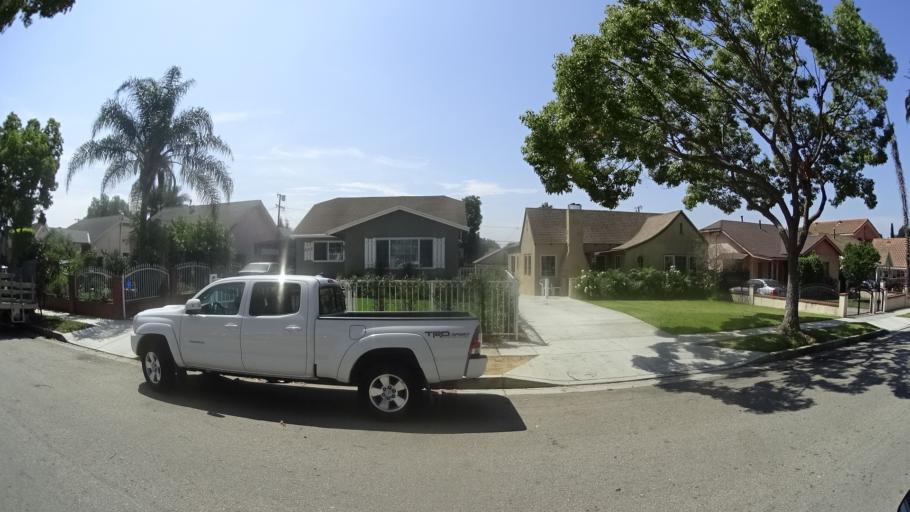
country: US
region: California
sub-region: Los Angeles County
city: View Park-Windsor Hills
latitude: 33.9800
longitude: -118.3434
